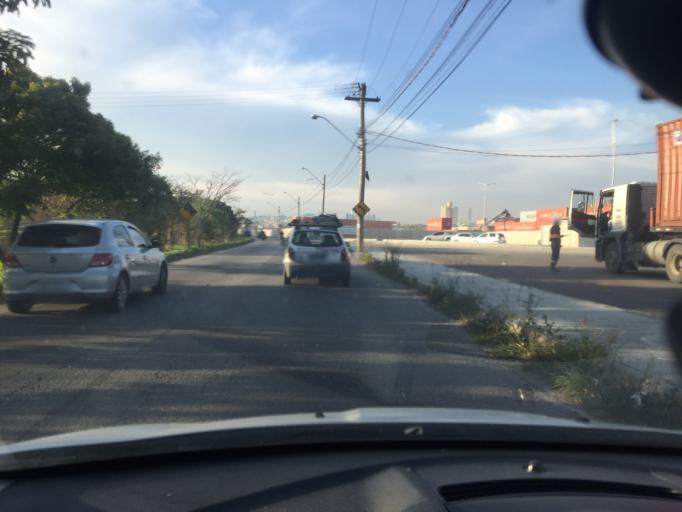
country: BR
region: Sao Paulo
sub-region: Jundiai
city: Jundiai
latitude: -23.1964
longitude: -46.8683
